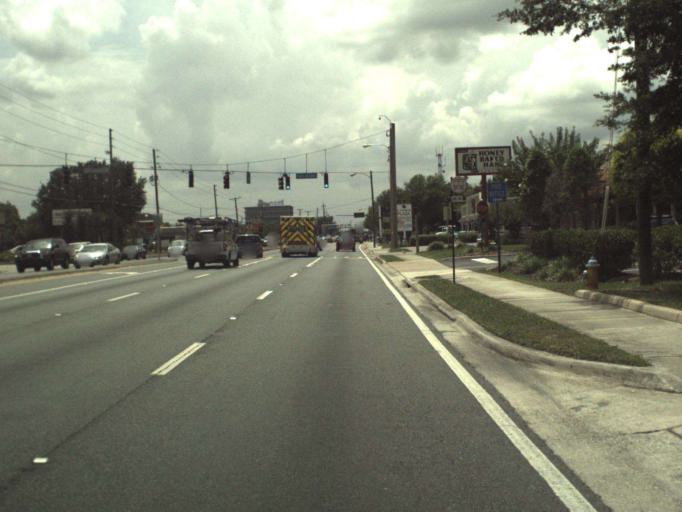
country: US
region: Florida
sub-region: Seminole County
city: Altamonte Springs
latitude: 28.6632
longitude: -81.3523
